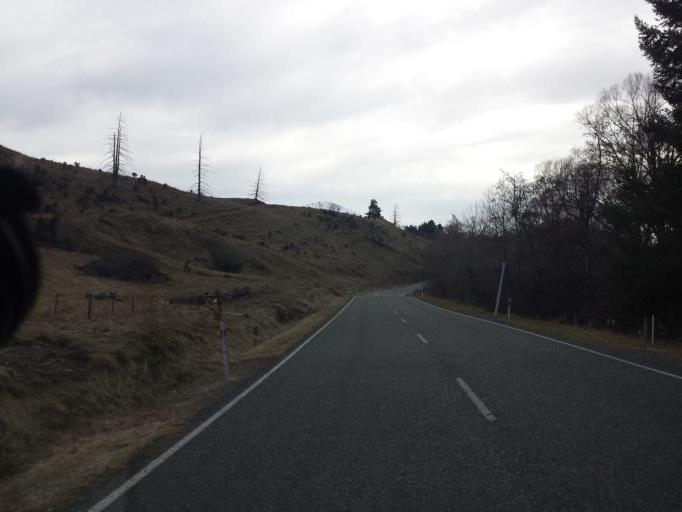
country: NZ
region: Canterbury
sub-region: Timaru District
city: Pleasant Point
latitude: -44.0576
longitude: 170.6757
